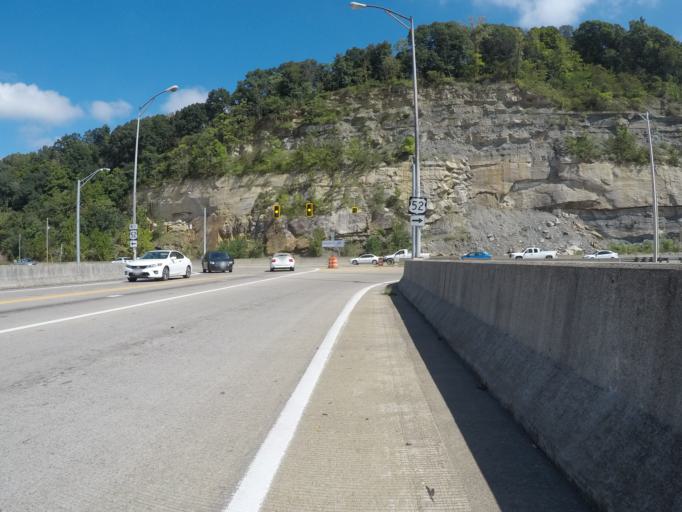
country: US
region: Kentucky
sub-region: Boyd County
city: Ashland
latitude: 38.4861
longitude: -82.6386
